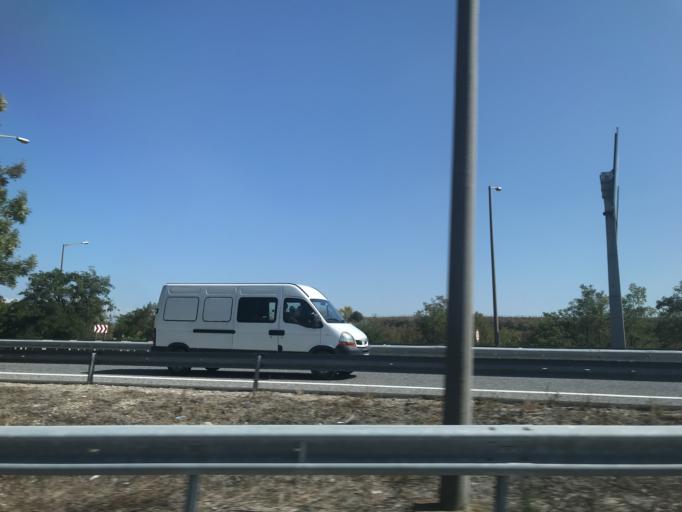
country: TR
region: Kirklareli
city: Luleburgaz
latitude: 41.4480
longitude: 27.3896
